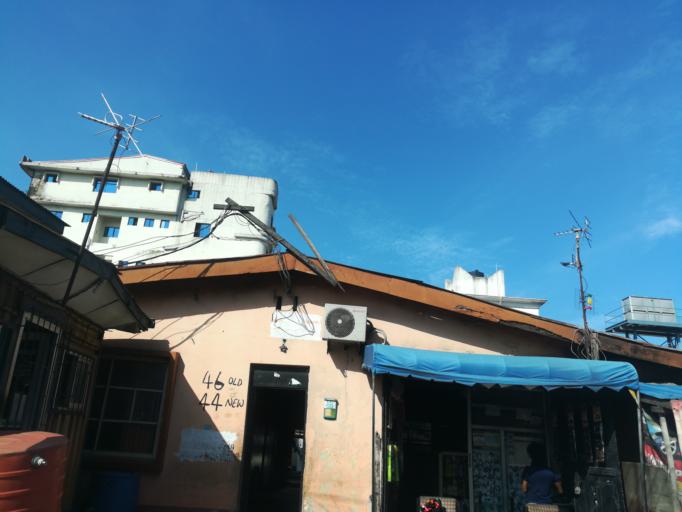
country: NG
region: Lagos
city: Ikeja
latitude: 6.6006
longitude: 3.3398
